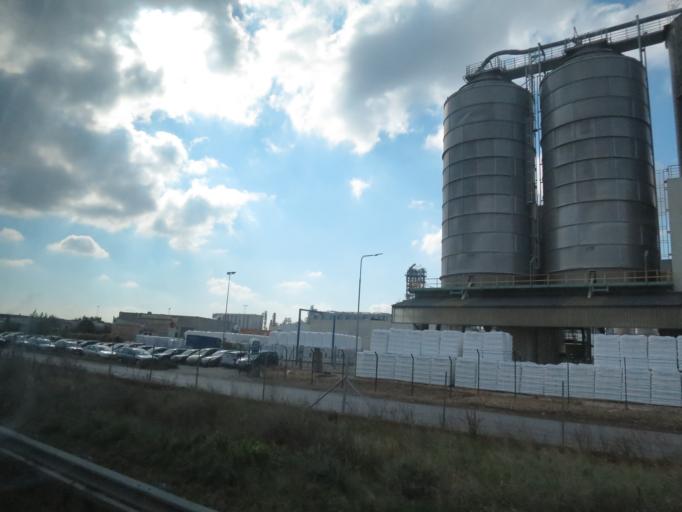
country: AT
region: Lower Austria
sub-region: Politischer Bezirk Wien-Umgebung
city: Schwechat
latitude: 48.1433
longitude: 16.5149
